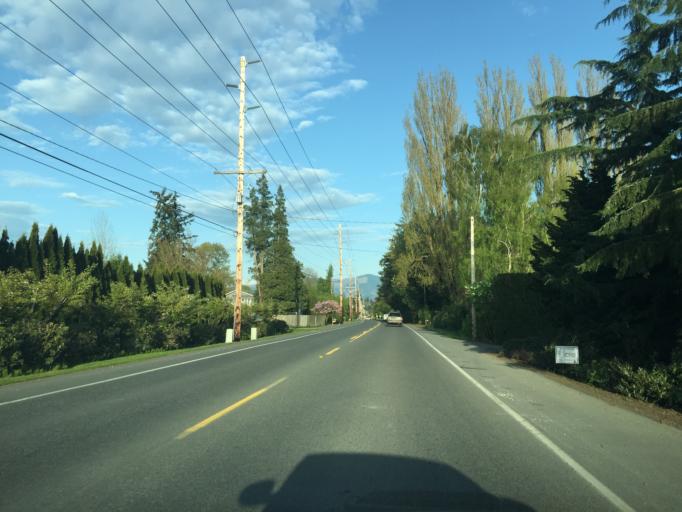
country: US
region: Washington
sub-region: Skagit County
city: Mount Vernon
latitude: 48.4207
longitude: -122.3587
